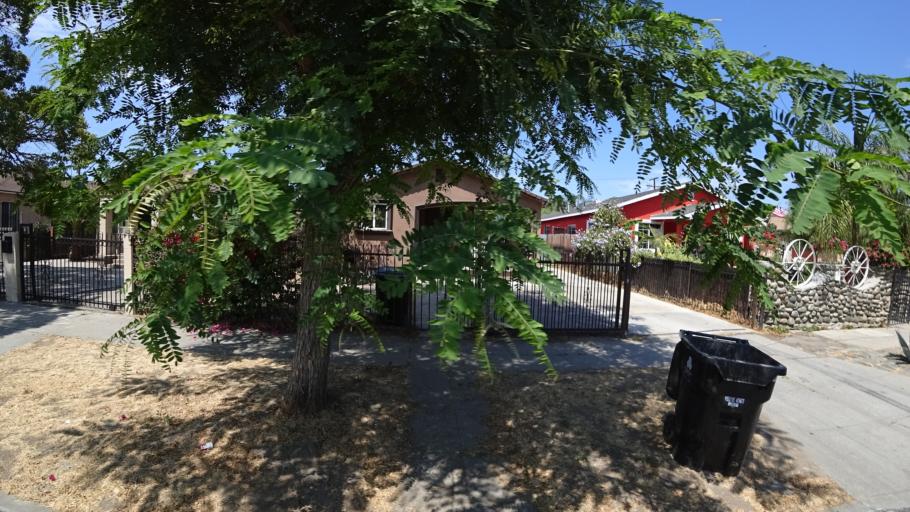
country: US
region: California
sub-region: Los Angeles County
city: Westmont
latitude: 33.9557
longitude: -118.2882
